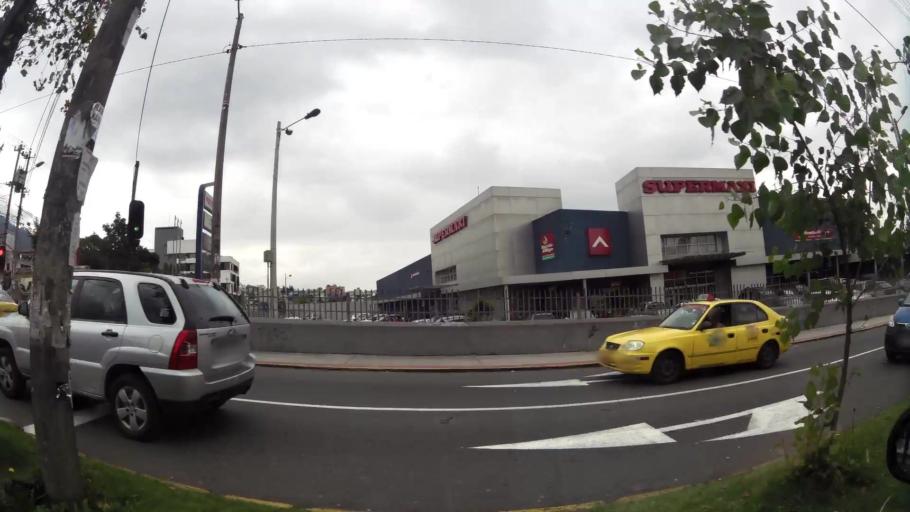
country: EC
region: Pichincha
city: Quito
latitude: -0.1967
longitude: -78.5018
